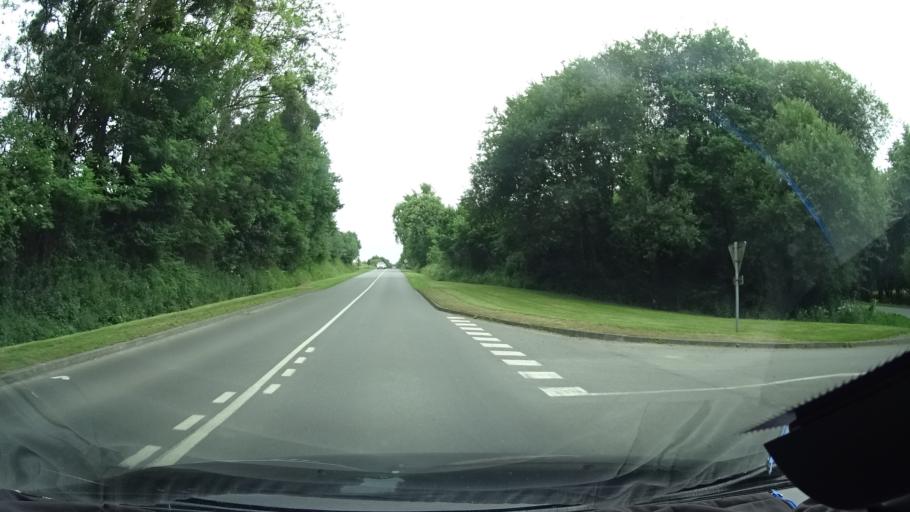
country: FR
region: Brittany
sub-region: Departement d'Ille-et-Vilaine
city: Le Minihic-sur-Rance
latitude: 48.5719
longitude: -2.0163
